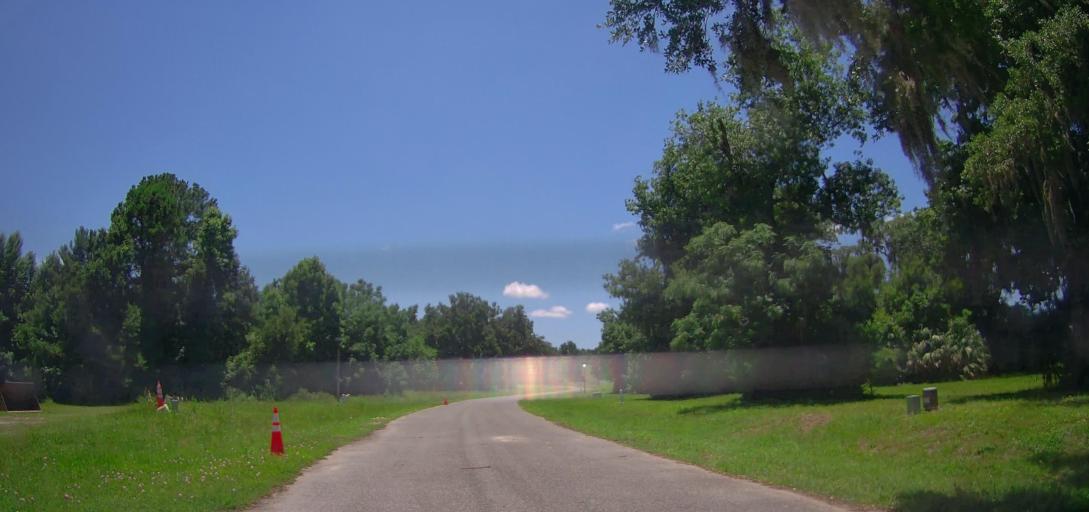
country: US
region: Florida
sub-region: Marion County
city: Belleview
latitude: 29.0907
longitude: -82.0741
